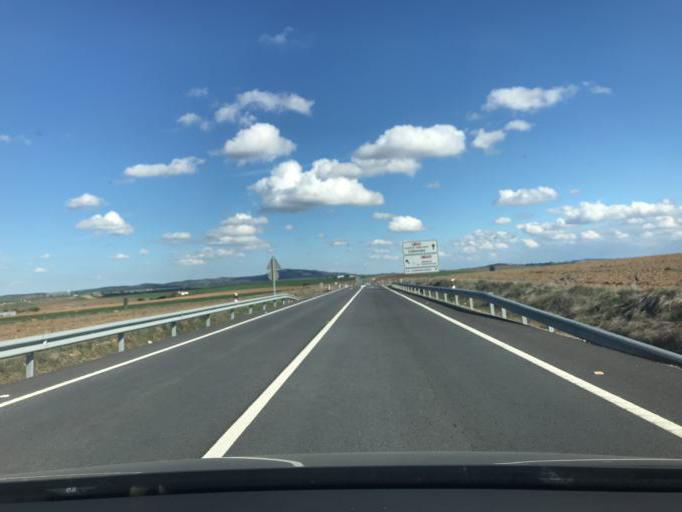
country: ES
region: Extremadura
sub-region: Provincia de Badajoz
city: Granja de Torrehermosa
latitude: 38.3000
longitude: -5.5877
